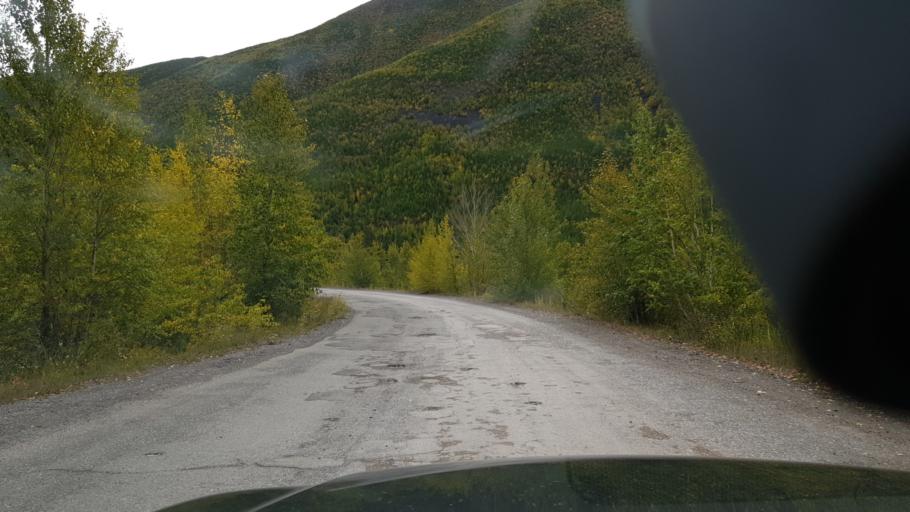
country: US
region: Montana
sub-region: Flathead County
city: Columbia Falls
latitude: 48.6206
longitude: -114.1417
